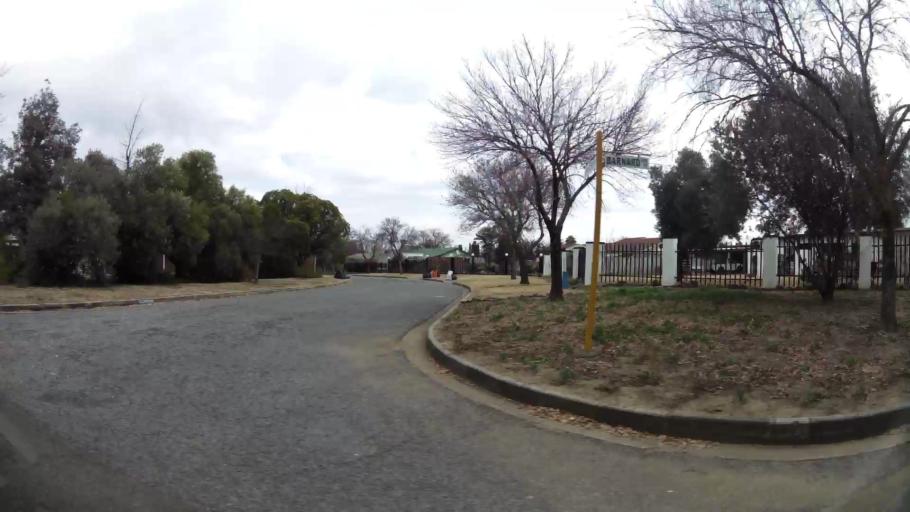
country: ZA
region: Orange Free State
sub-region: Fezile Dabi District Municipality
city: Kroonstad
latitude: -27.6799
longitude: 27.2477
